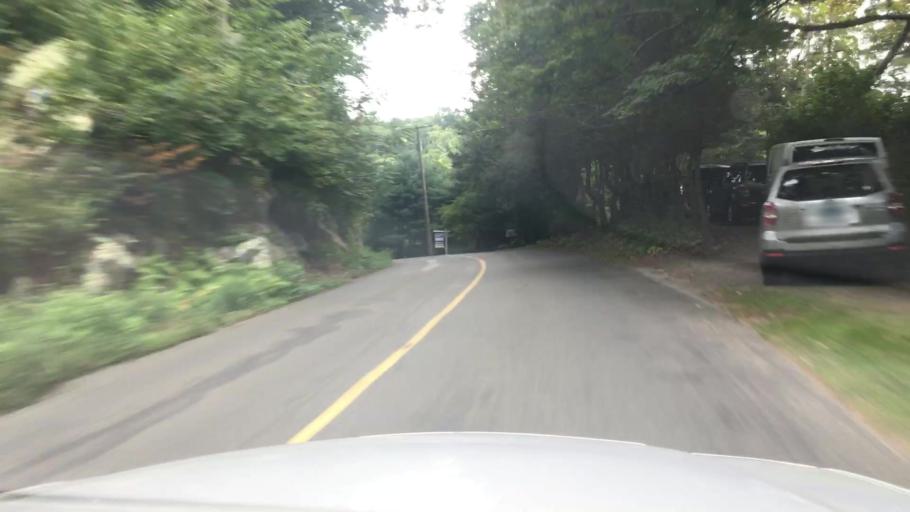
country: US
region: Connecticut
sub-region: Middlesex County
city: Deep River Center
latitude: 41.3841
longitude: -72.4158
